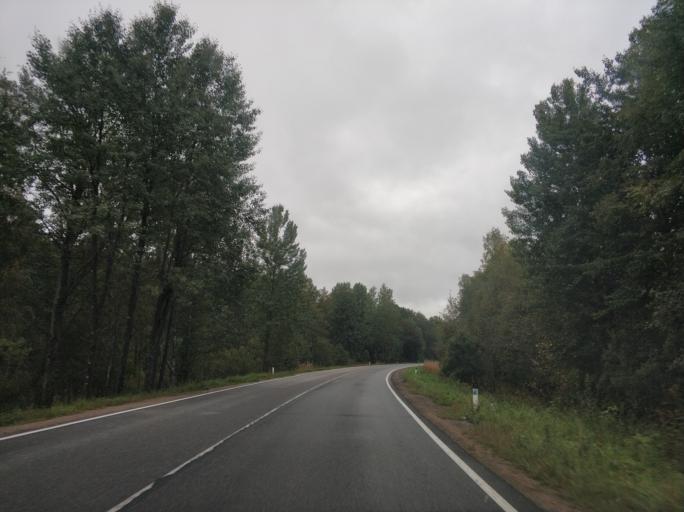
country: RU
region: Leningrad
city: Borisova Griva
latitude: 60.1334
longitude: 30.9619
